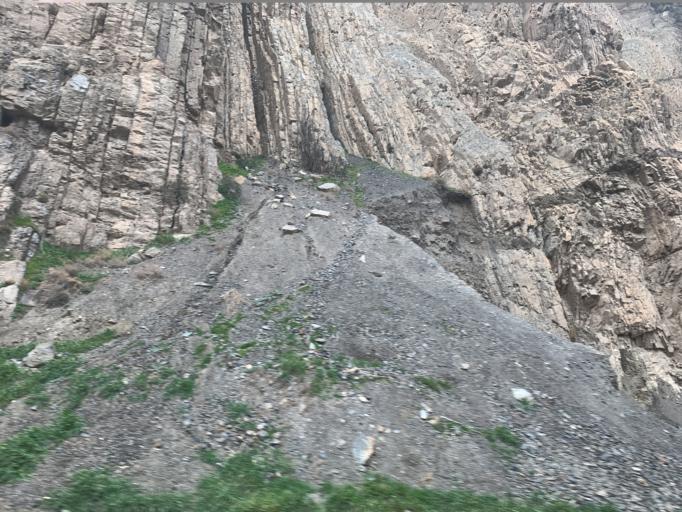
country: IR
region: Mazandaran
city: Amol
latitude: 36.1119
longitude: 52.2807
